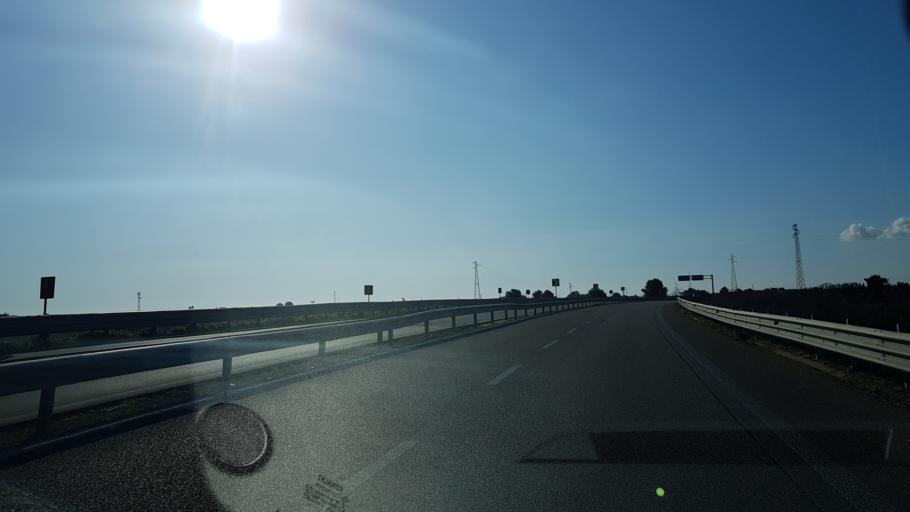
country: IT
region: Apulia
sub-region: Provincia di Lecce
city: Galatone
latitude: 40.1279
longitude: 18.0532
